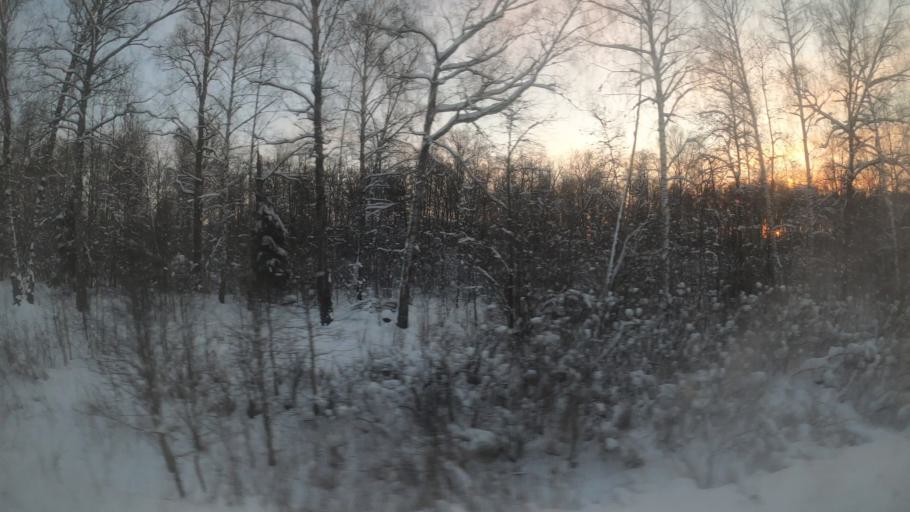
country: RU
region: Moskovskaya
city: Podosinki
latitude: 56.2128
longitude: 37.5269
